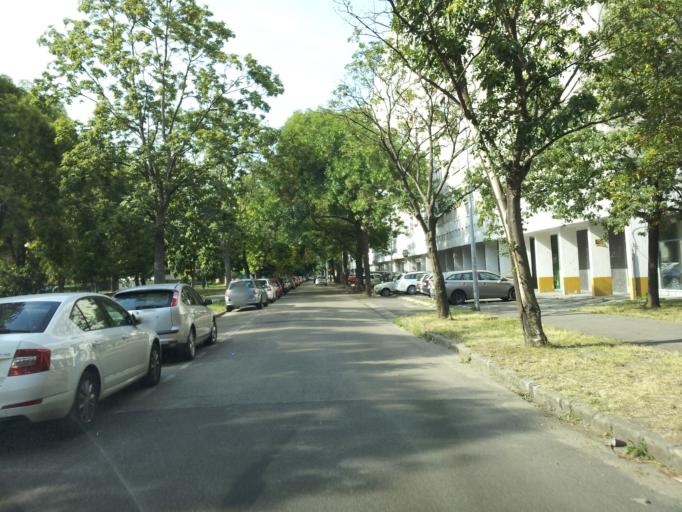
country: HU
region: Budapest
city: Budapest III. keruelet
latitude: 47.5392
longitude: 19.0358
